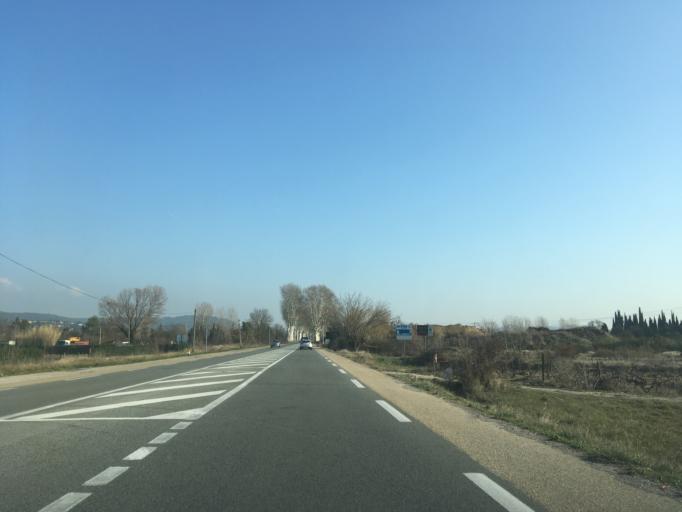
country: FR
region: Provence-Alpes-Cote d'Azur
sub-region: Departement du Var
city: Vidauban
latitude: 43.4386
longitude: 6.4500
